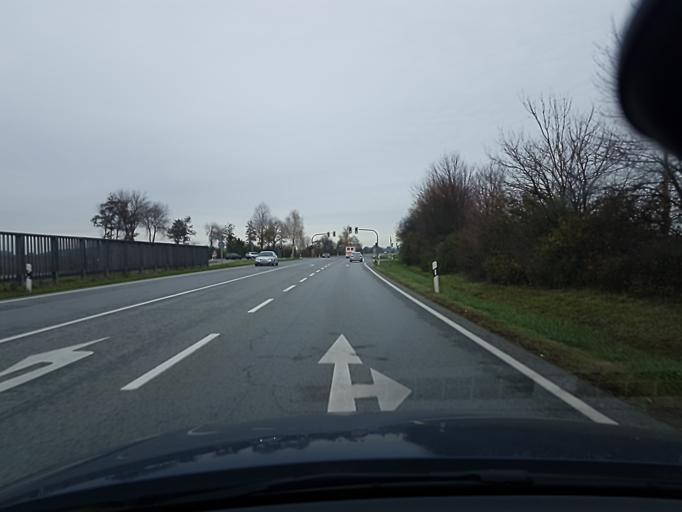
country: DE
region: Bavaria
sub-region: Lower Bavaria
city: Ergolding
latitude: 48.5891
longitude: 12.1897
